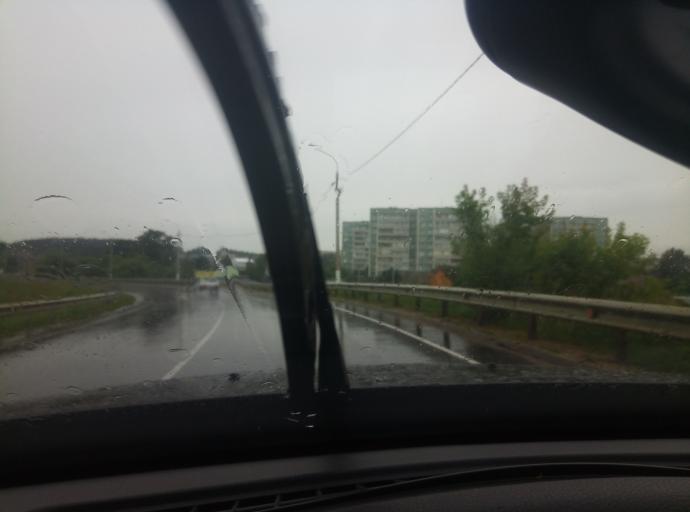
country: RU
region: Kaluga
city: Kremenki
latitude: 54.8814
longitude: 37.1250
